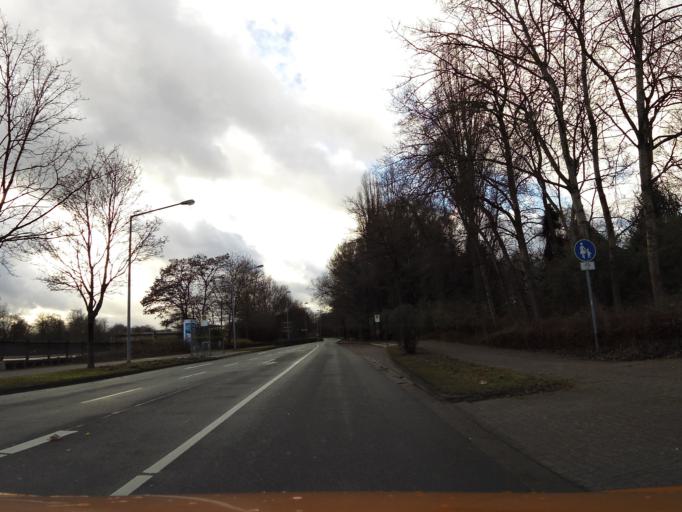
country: DE
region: Lower Saxony
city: Oldenburg
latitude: 53.1304
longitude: 8.2159
